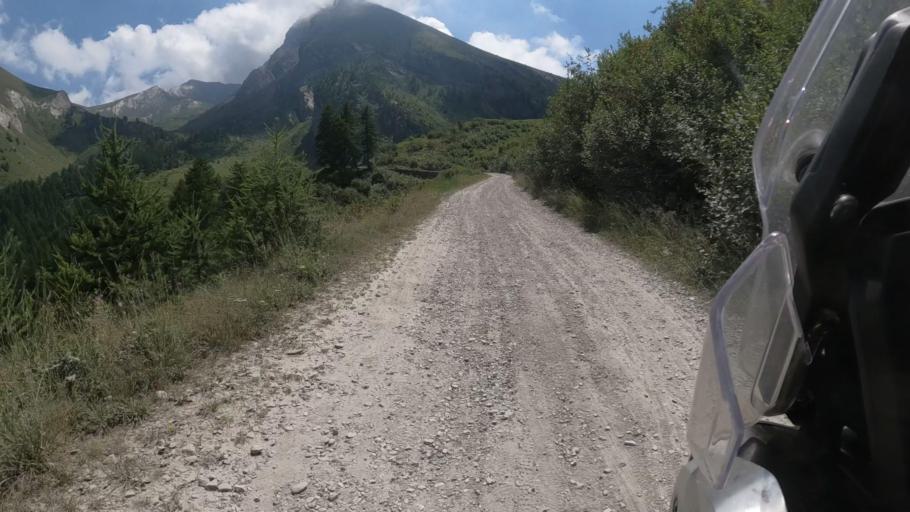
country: IT
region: Piedmont
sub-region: Provincia di Torino
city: Usseaux
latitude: 45.0800
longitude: 7.0538
